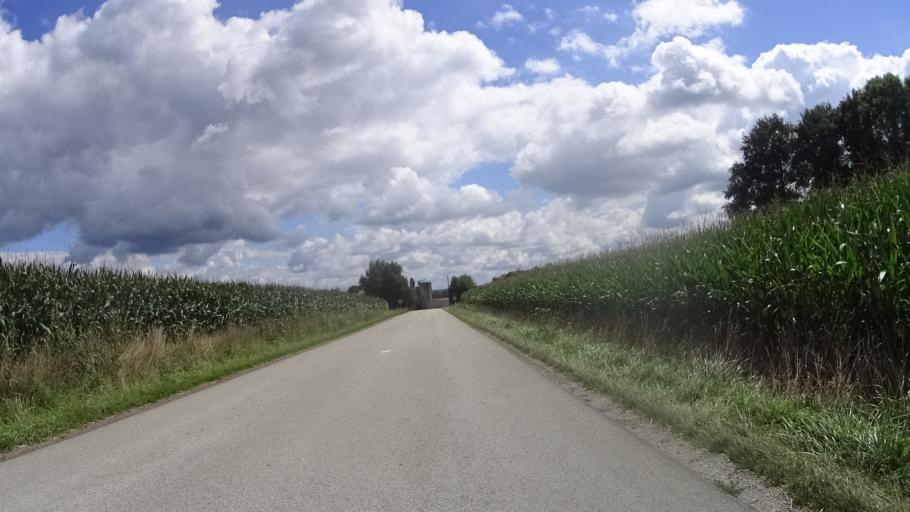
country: FR
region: Champagne-Ardenne
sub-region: Departement de la Haute-Marne
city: Montier-en-Der
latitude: 48.4632
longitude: 4.7445
